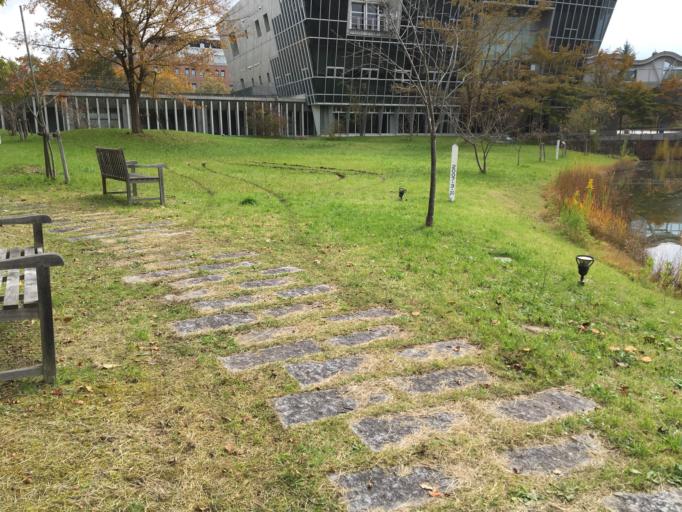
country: JP
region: Miyagi
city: Tomiya
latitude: 38.3500
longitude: 140.8410
